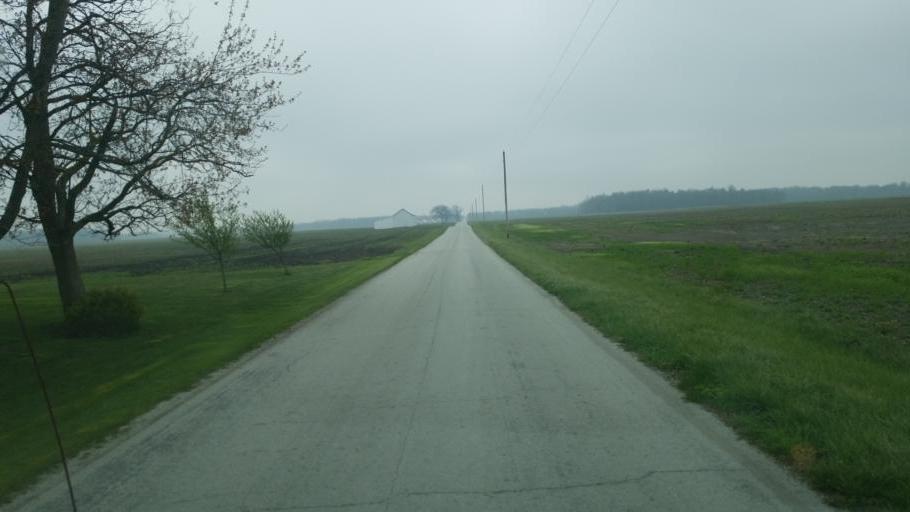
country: US
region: Ohio
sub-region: Hardin County
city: Forest
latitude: 40.6710
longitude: -83.4398
